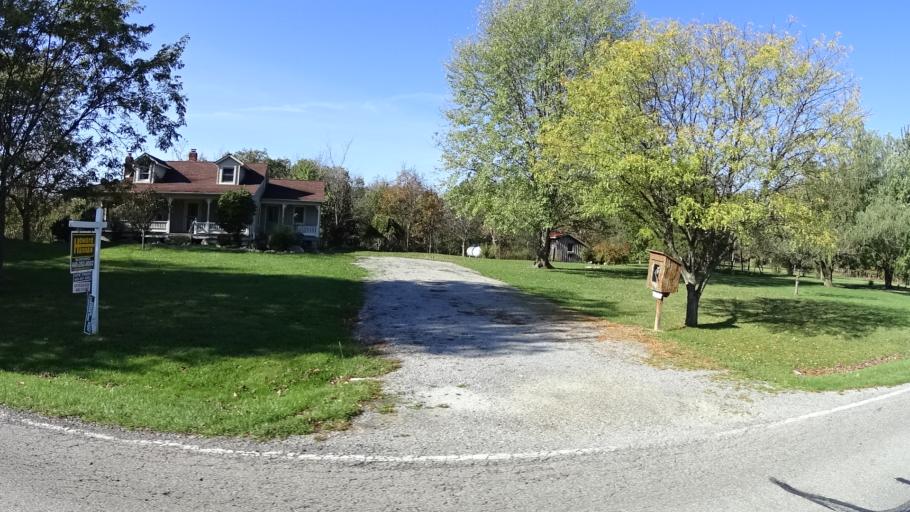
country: US
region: Ohio
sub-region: Lorain County
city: Vermilion-on-the-Lake
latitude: 41.3911
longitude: -82.3227
